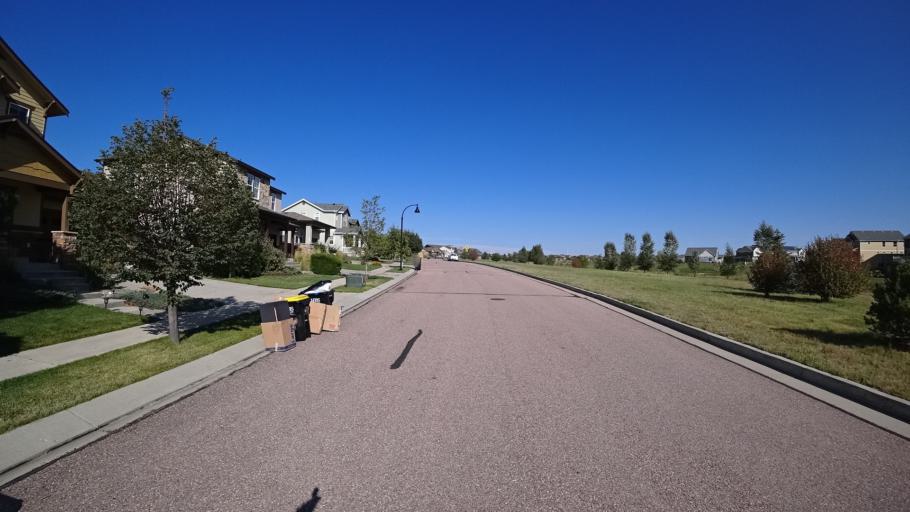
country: US
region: Colorado
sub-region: El Paso County
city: Cimarron Hills
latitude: 38.9305
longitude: -104.6714
